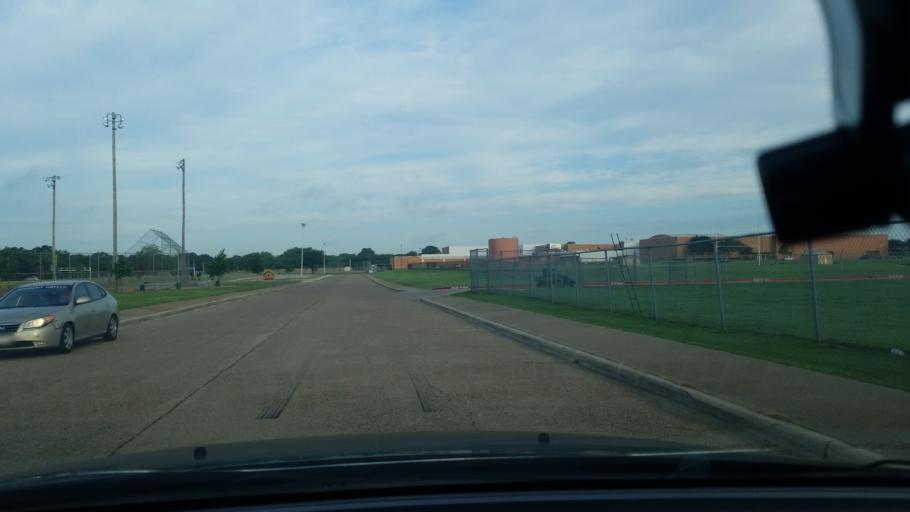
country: US
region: Texas
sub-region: Dallas County
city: Balch Springs
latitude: 32.7599
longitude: -96.6321
